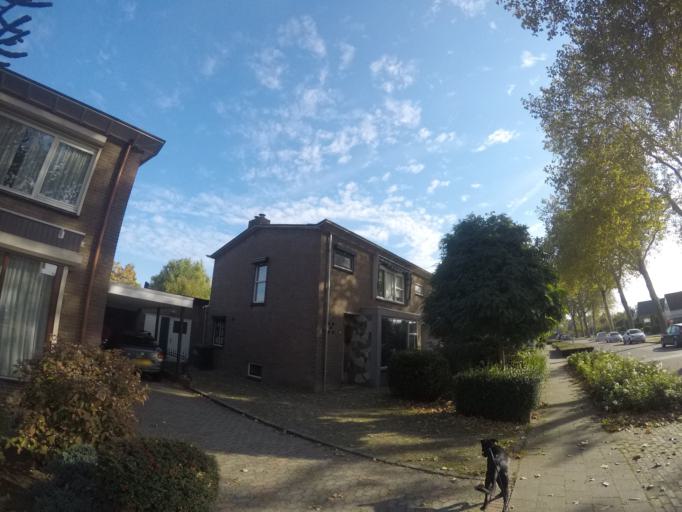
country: NL
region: Gelderland
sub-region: Gemeente Zevenaar
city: Zevenaar
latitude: 51.9275
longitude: 6.0668
